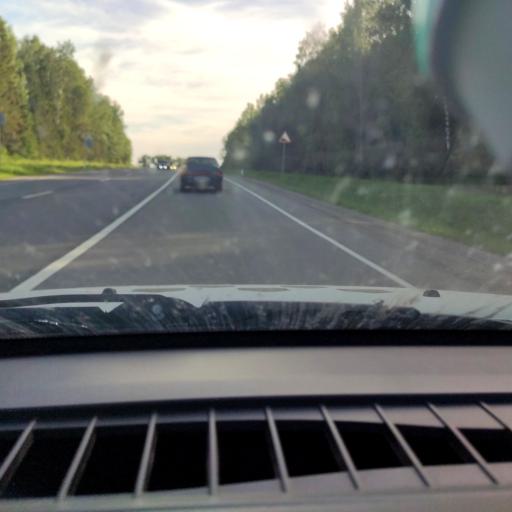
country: RU
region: Kirov
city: Vakhrushi
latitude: 58.6643
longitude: 49.9275
